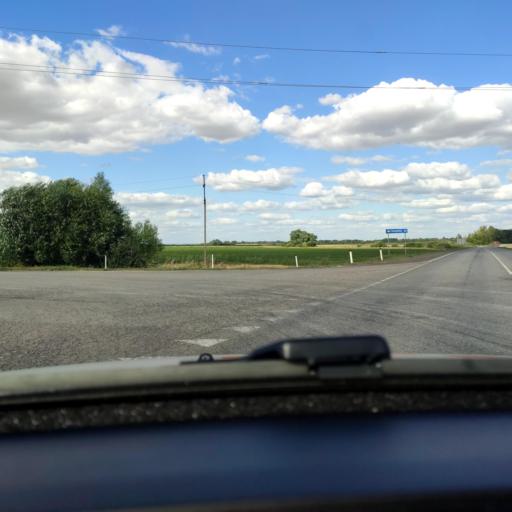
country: RU
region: Voronezj
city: Kashirskoye
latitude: 51.4670
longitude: 39.8637
